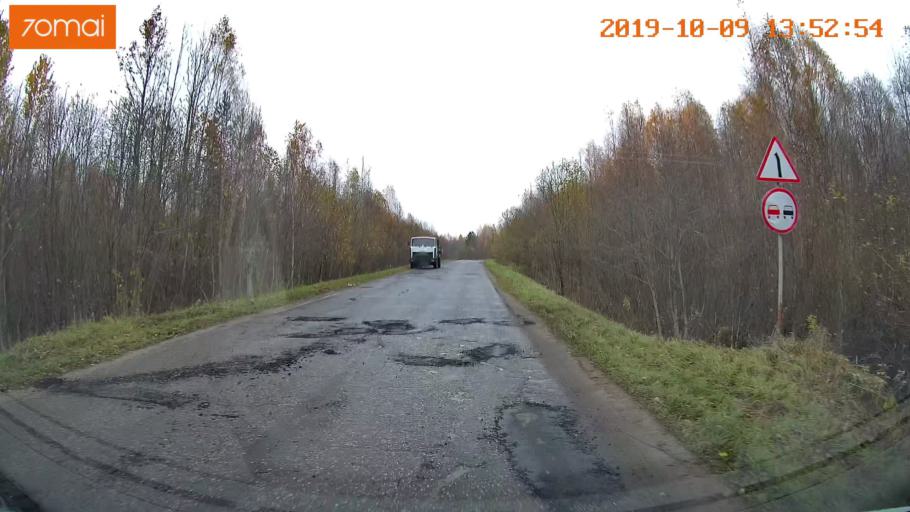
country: RU
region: Kostroma
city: Buy
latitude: 58.4129
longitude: 41.2528
